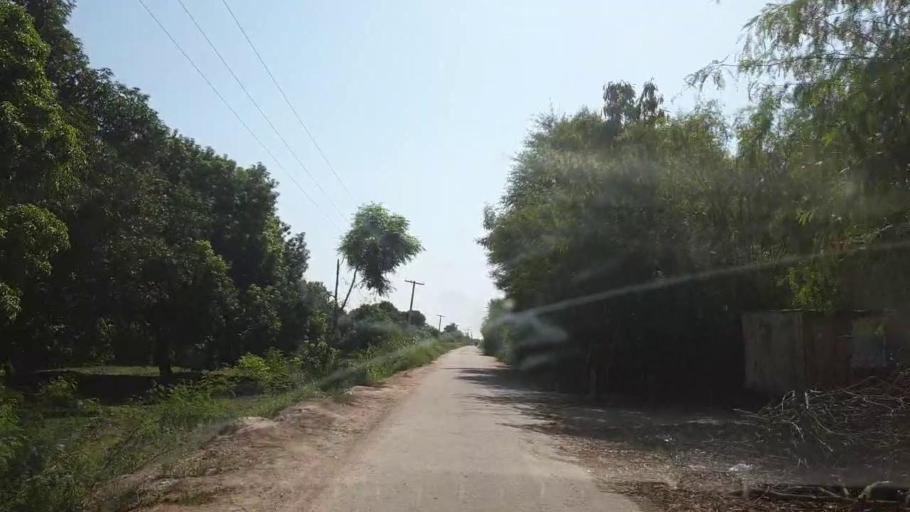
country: PK
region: Sindh
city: Tando Jam
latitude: 25.4378
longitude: 68.5845
